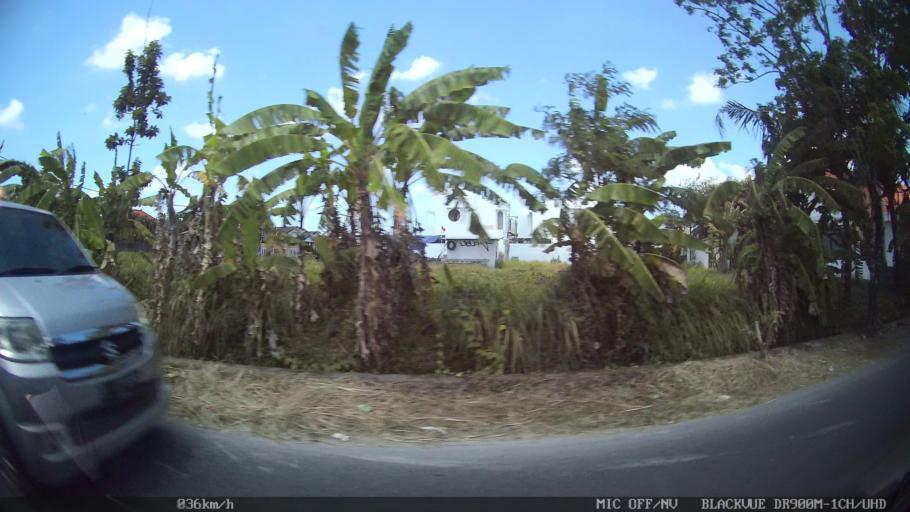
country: ID
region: Bali
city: Banjar Gunungpande
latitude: -8.6517
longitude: 115.1575
